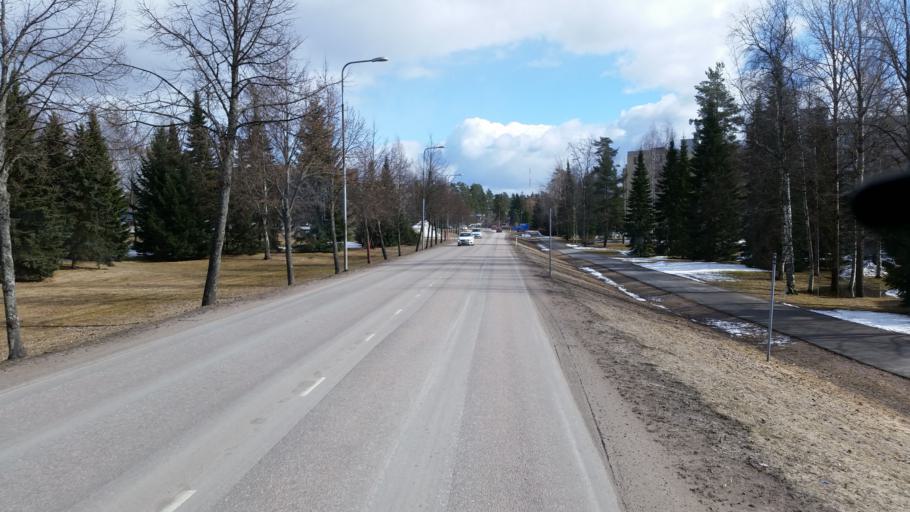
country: FI
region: South Karelia
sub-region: Imatra
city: Imatra
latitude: 61.1705
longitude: 28.7598
